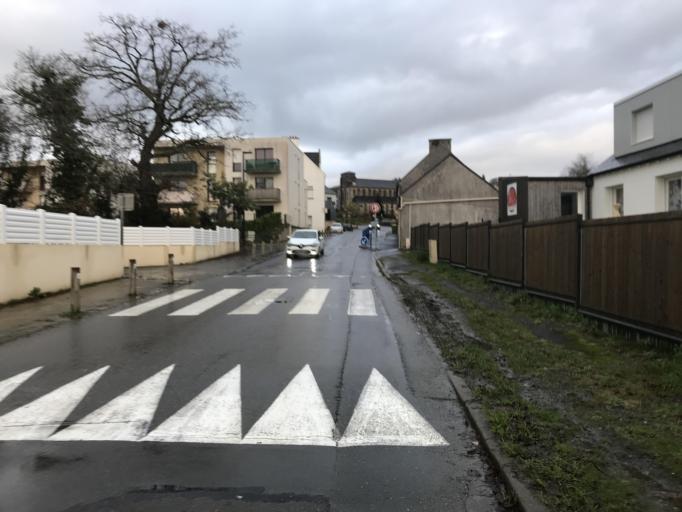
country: FR
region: Brittany
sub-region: Departement du Finistere
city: Loperhet
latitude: 48.3732
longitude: -4.3068
